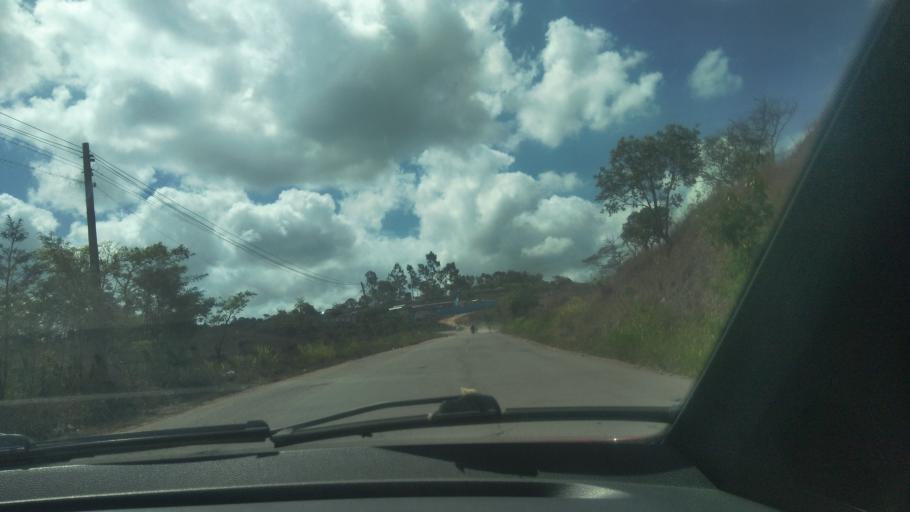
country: BR
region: Pernambuco
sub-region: Vitoria De Santo Antao
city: Vitoria de Santo Antao
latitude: -8.1361
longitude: -35.2763
